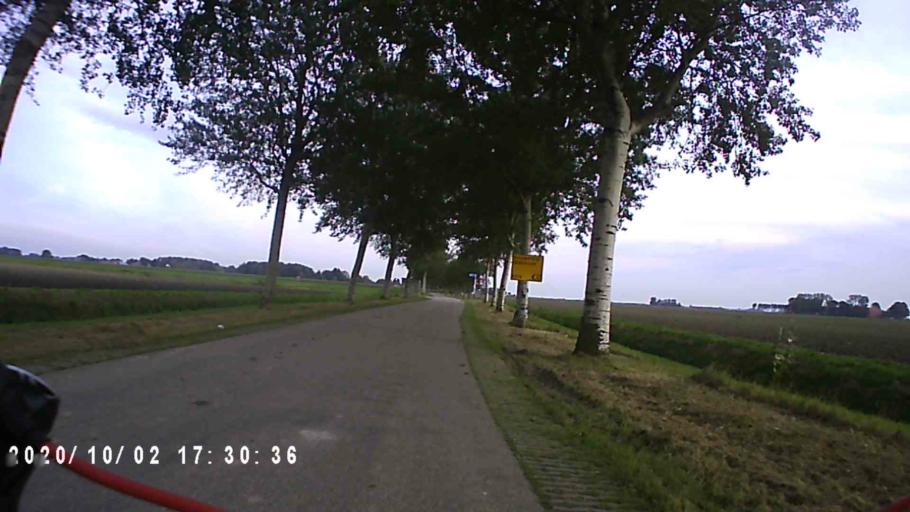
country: NL
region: Groningen
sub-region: Gemeente De Marne
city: Ulrum
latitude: 53.3371
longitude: 6.3281
